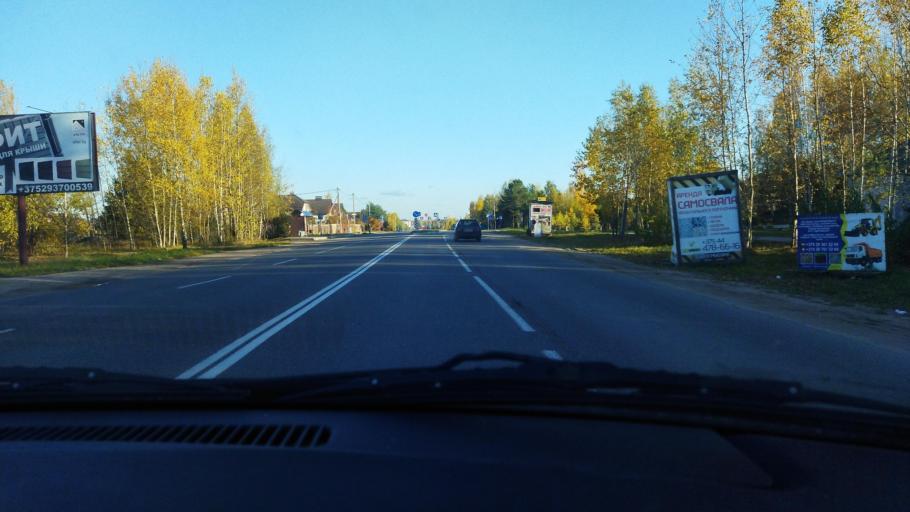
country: BY
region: Minsk
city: Kalodzishchy
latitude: 53.9187
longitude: 27.7542
